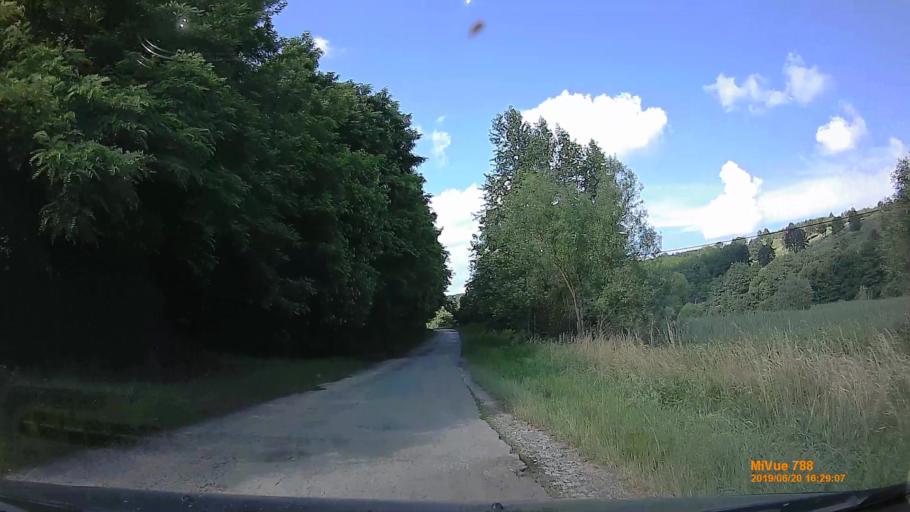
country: HU
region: Baranya
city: Buekkoesd
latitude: 46.1591
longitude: 18.0575
